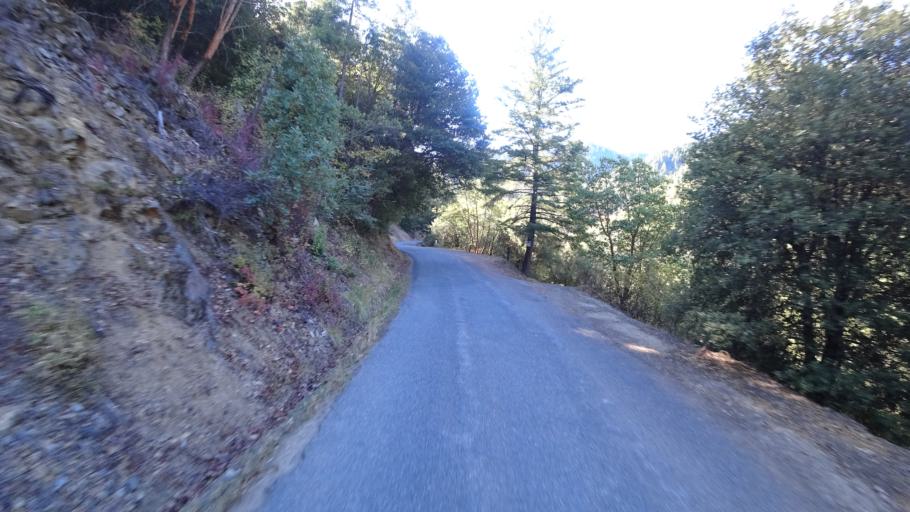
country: US
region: California
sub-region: Humboldt County
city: Willow Creek
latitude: 41.1742
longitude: -123.2193
